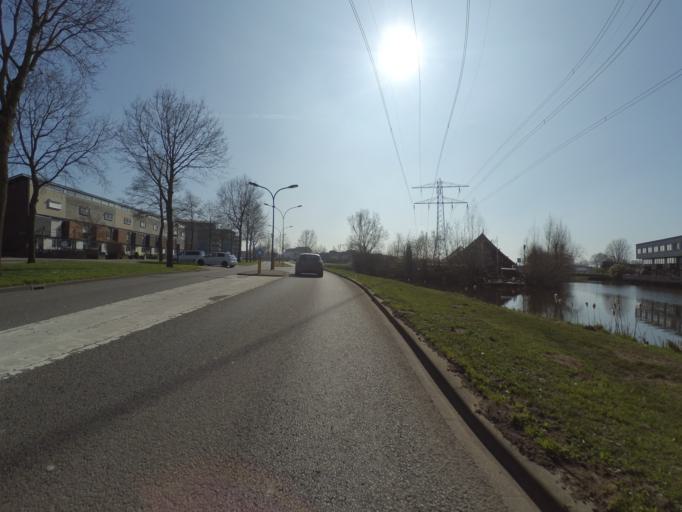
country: NL
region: Utrecht
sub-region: Gemeente Amersfoort
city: Hoogland
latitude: 52.2020
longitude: 5.3688
